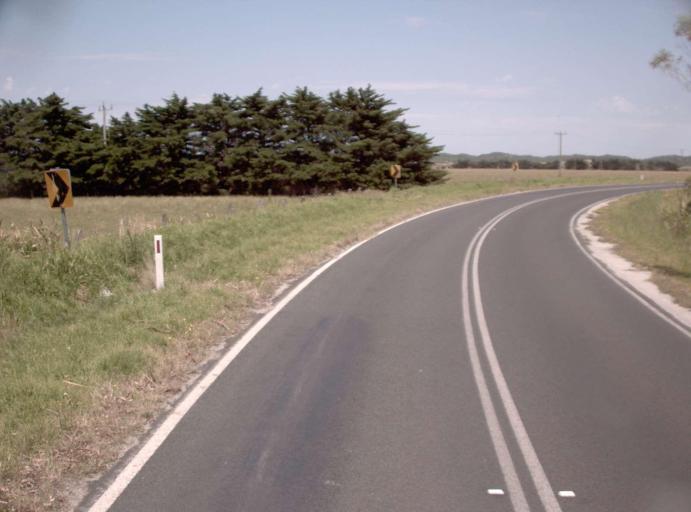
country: AU
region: Victoria
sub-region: Bass Coast
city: North Wonthaggi
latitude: -38.7001
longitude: 145.8534
